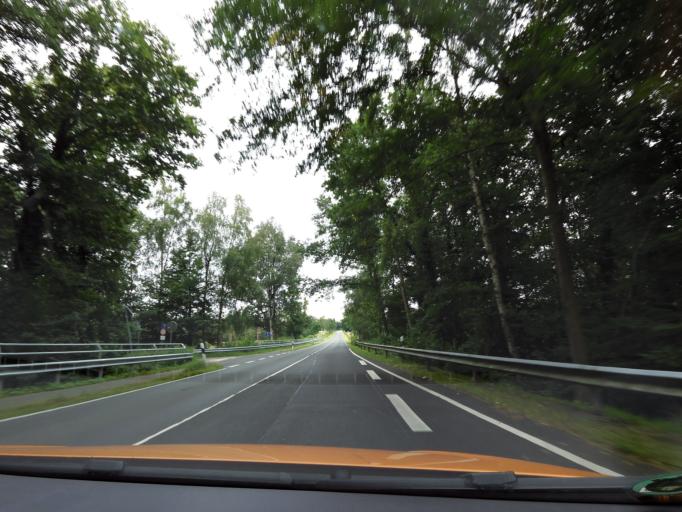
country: DE
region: Lower Saxony
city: Westerstede
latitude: 53.2516
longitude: 7.9708
